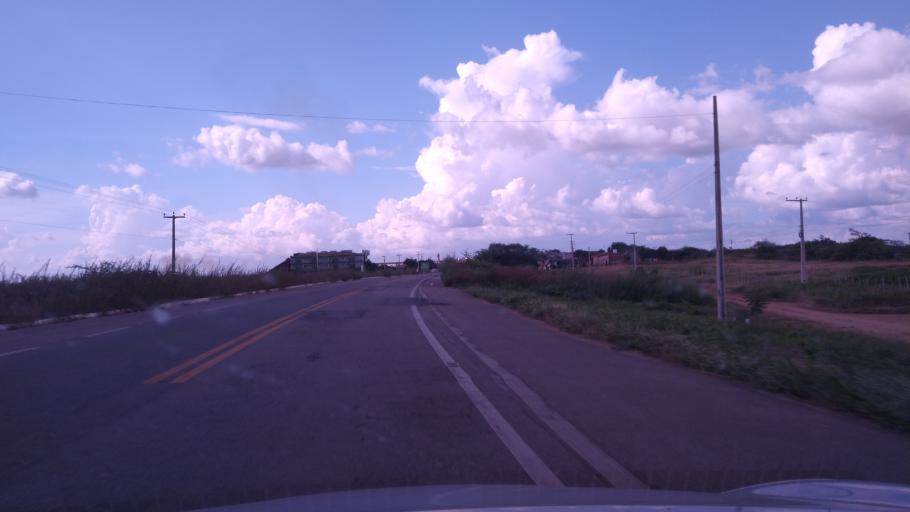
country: BR
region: Ceara
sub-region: Caninde
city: Caninde
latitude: -4.3860
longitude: -39.3123
